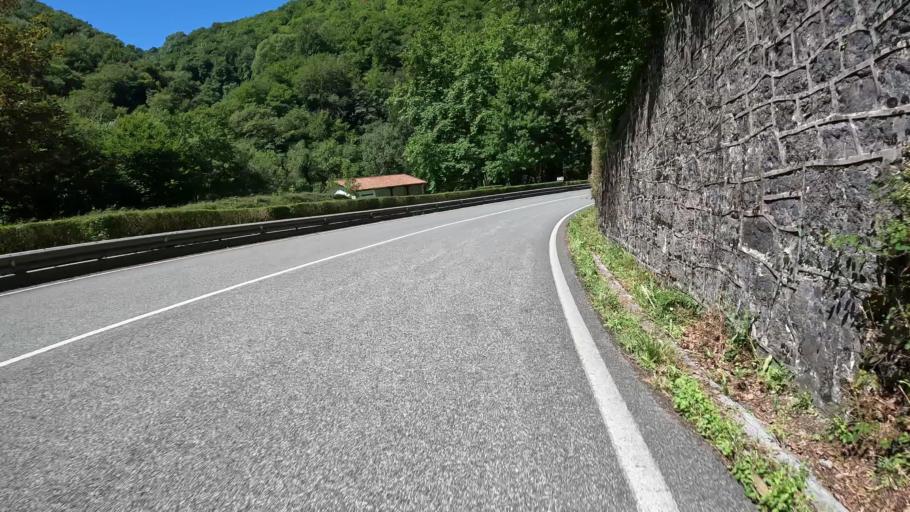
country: ES
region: Basque Country
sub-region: Provincia de Guipuzcoa
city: Oreja
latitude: 43.0698
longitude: -2.0103
